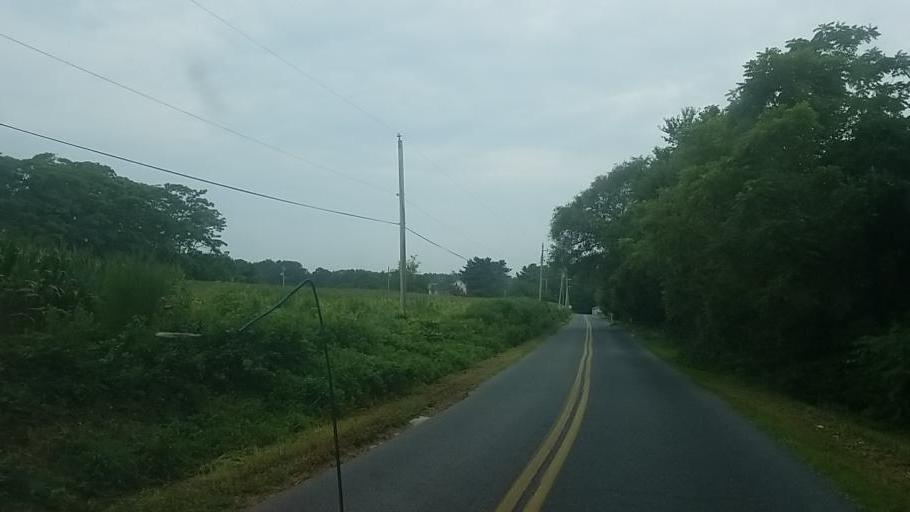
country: US
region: Delaware
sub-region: Sussex County
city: Selbyville
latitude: 38.4400
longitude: -75.1933
